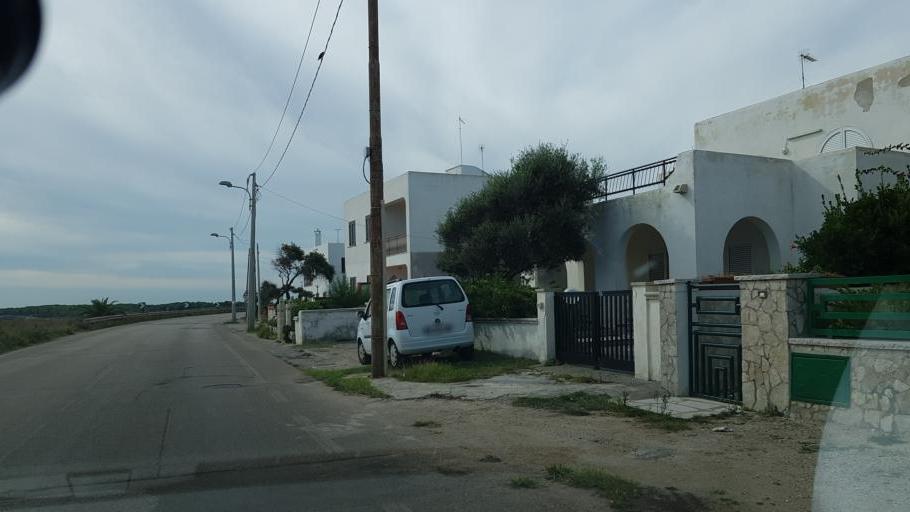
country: IT
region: Apulia
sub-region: Provincia di Lecce
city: Borgagne
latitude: 40.2803
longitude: 18.4313
